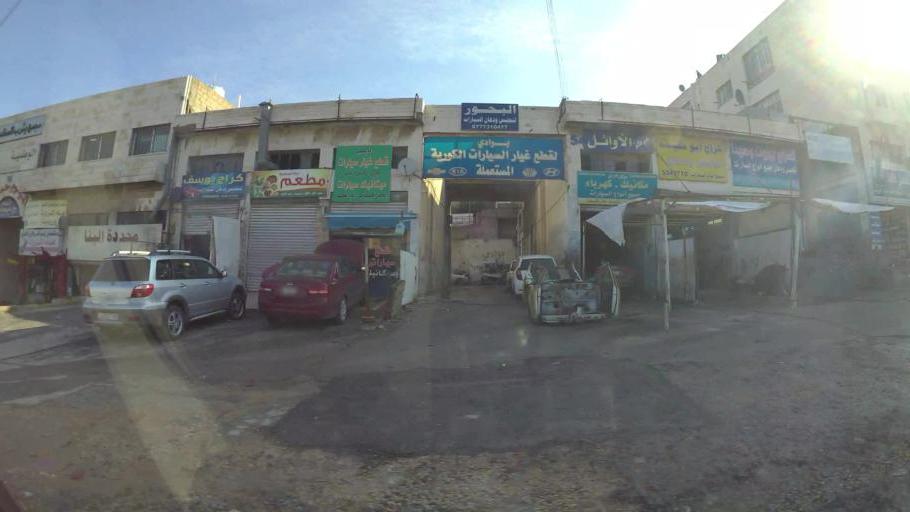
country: JO
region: Amman
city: Al Jubayhah
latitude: 32.0138
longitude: 35.8493
